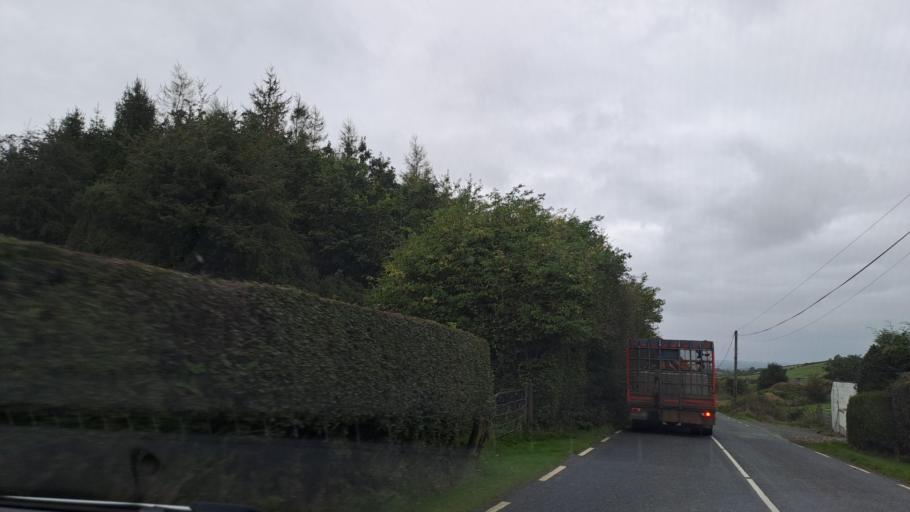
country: IE
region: Ulster
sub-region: County Monaghan
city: Castleblayney
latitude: 54.0890
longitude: -6.8319
